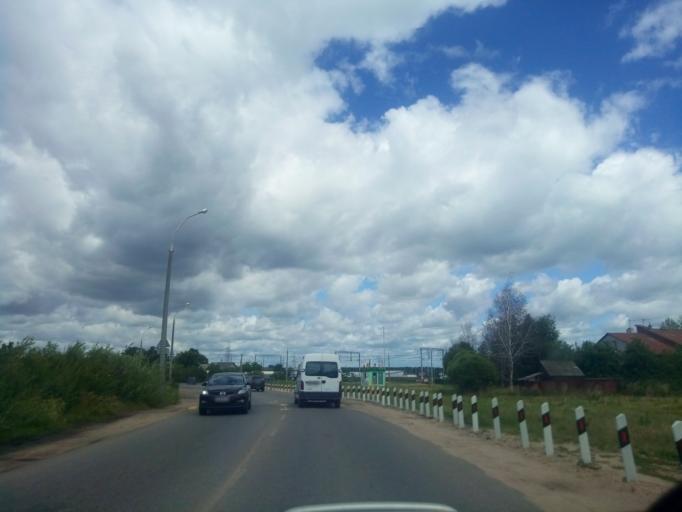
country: BY
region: Minsk
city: Zhdanovichy
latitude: 53.9395
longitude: 27.4361
